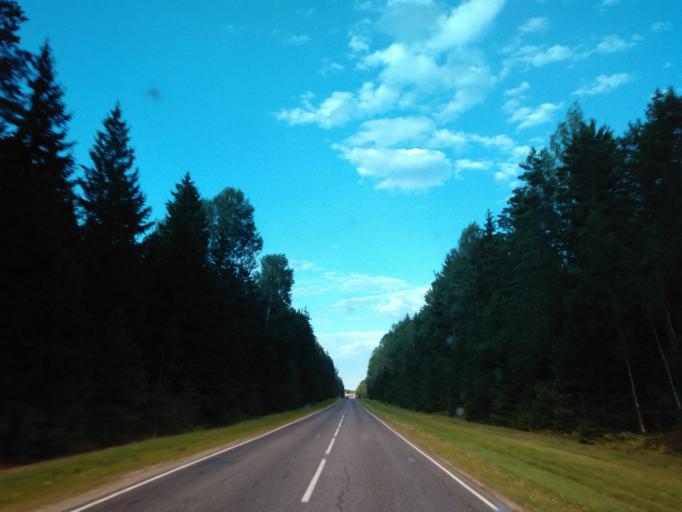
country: BY
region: Minsk
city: Uzda
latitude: 53.4325
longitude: 27.4722
